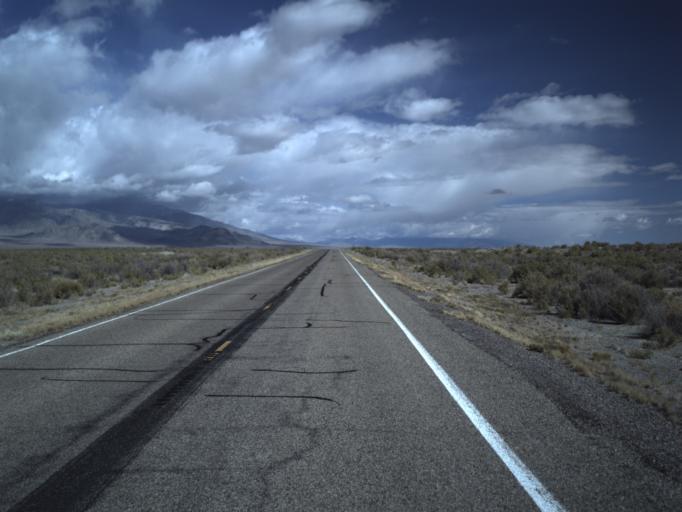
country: US
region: Nevada
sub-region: White Pine County
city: McGill
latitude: 39.0366
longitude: -114.0359
